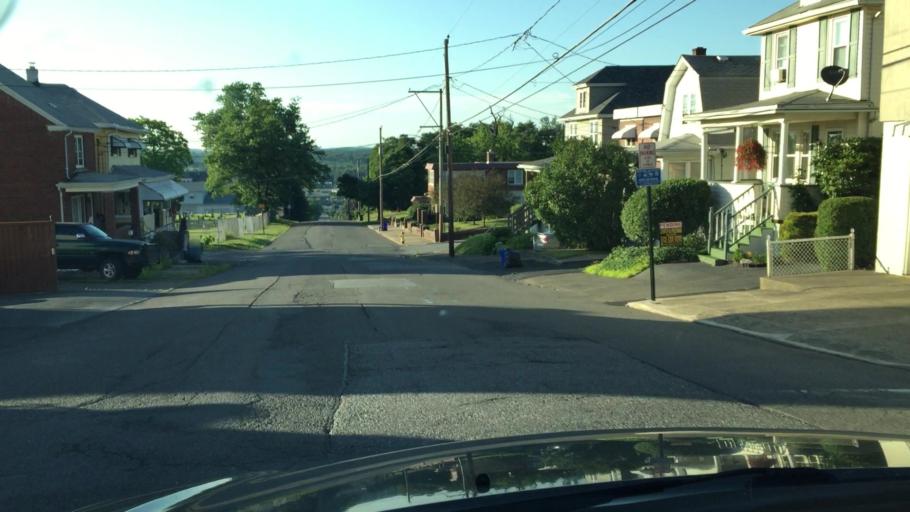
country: US
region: Pennsylvania
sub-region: Luzerne County
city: Hazleton
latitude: 40.9674
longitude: -75.9747
